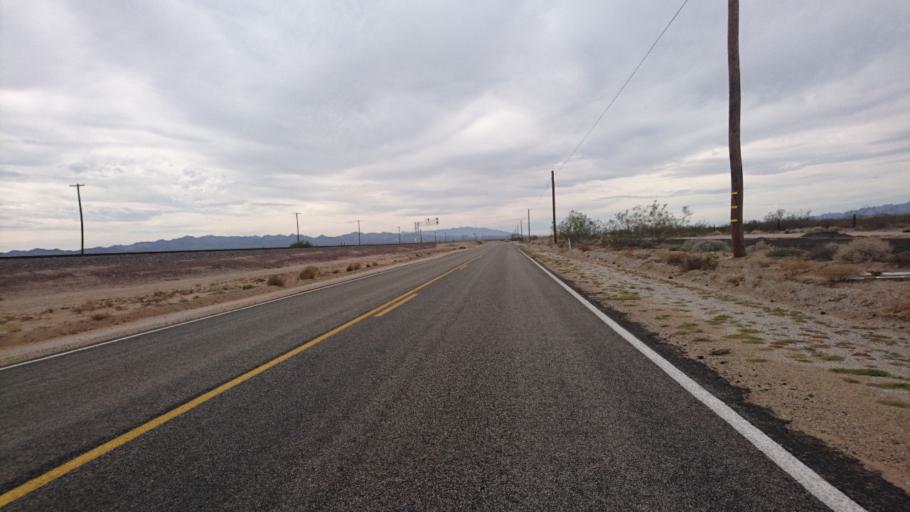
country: US
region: California
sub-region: San Bernardino County
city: Needles
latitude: 34.8968
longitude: -115.0937
